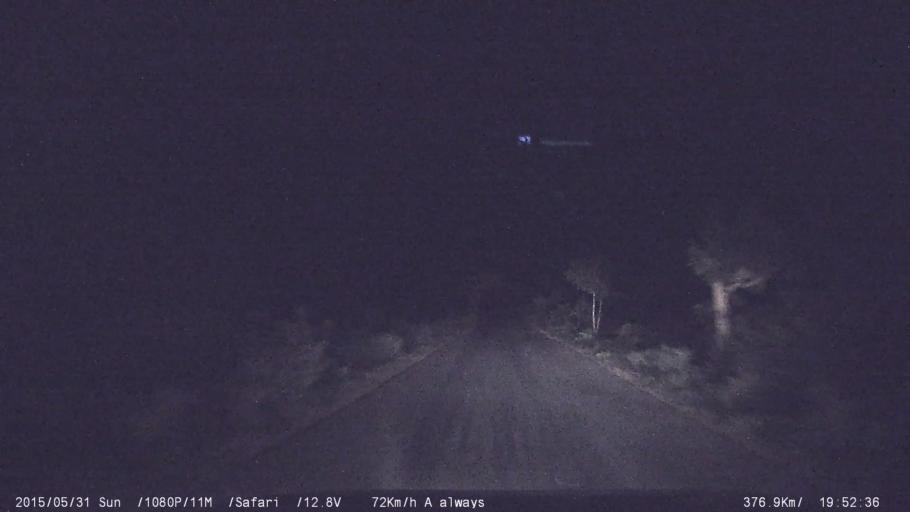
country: IN
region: Karnataka
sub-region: Mandya
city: Malavalli
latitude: 12.3364
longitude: 77.0764
